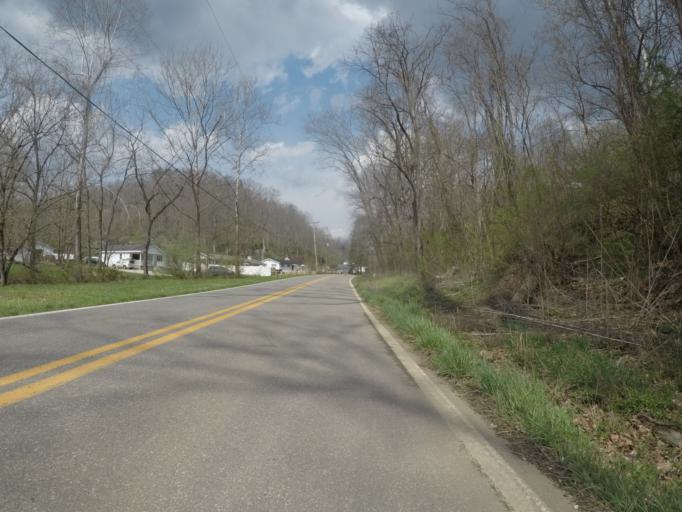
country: US
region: West Virginia
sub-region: Cabell County
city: Pea Ridge
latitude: 38.3373
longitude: -82.3398
